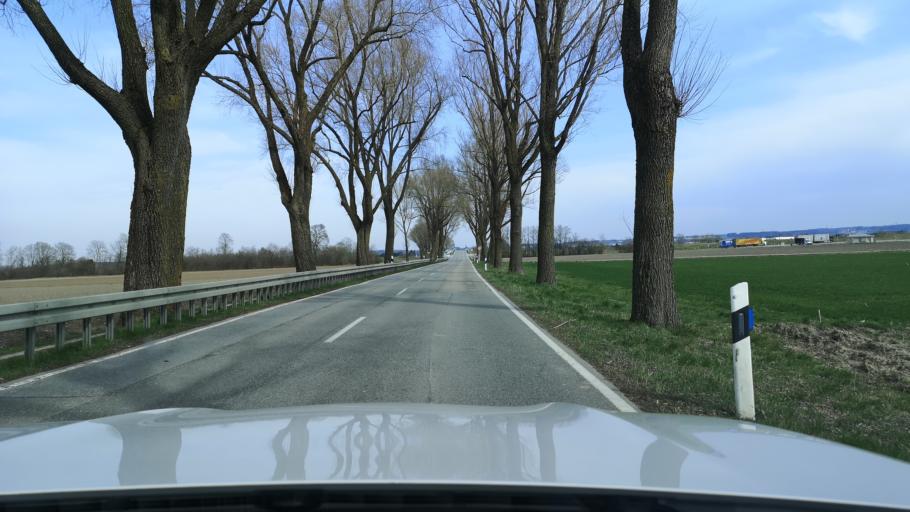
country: DE
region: Bavaria
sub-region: Upper Bavaria
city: Pastetten
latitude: 48.1969
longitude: 11.9199
